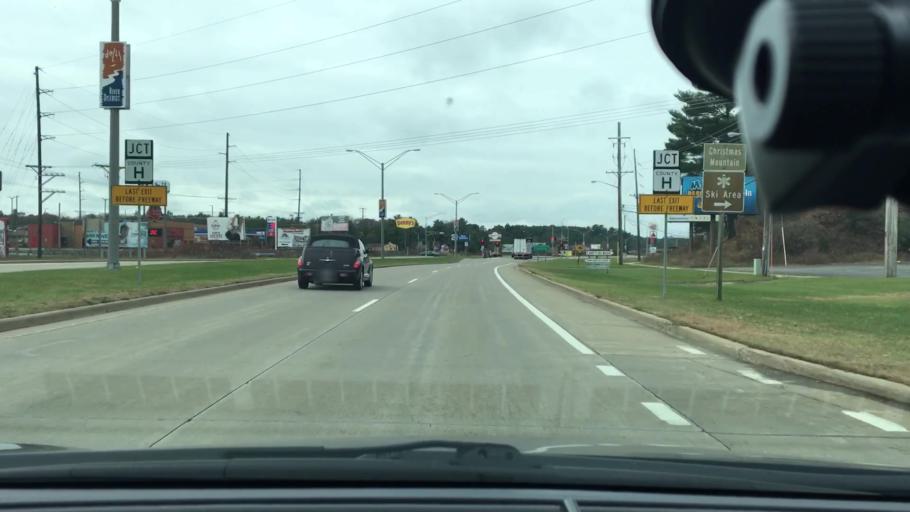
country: US
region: Wisconsin
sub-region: Columbia County
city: Wisconsin Dells
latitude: 43.6246
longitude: -89.7908
